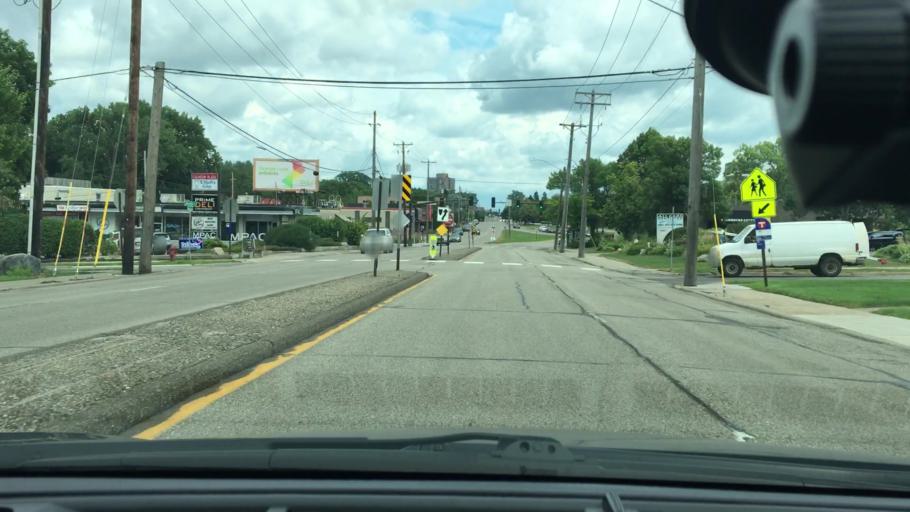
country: US
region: Minnesota
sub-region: Hennepin County
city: Saint Louis Park
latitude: 44.9484
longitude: -93.3344
